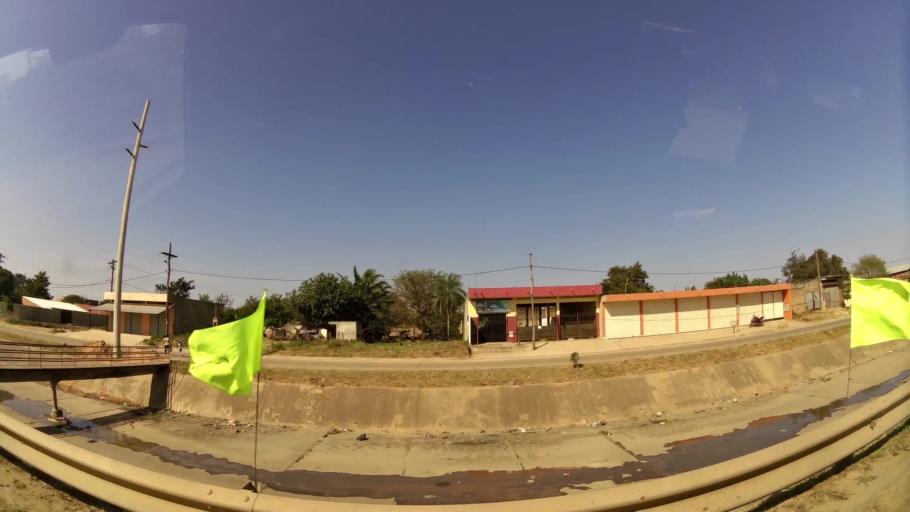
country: BO
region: Santa Cruz
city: Cotoca
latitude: -17.8009
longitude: -63.1095
